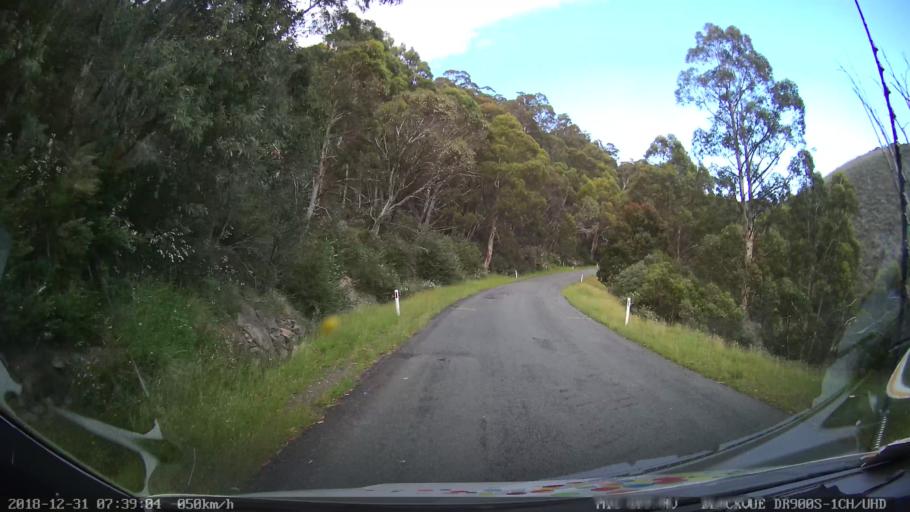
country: AU
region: New South Wales
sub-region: Snowy River
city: Jindabyne
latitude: -36.3503
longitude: 148.4242
